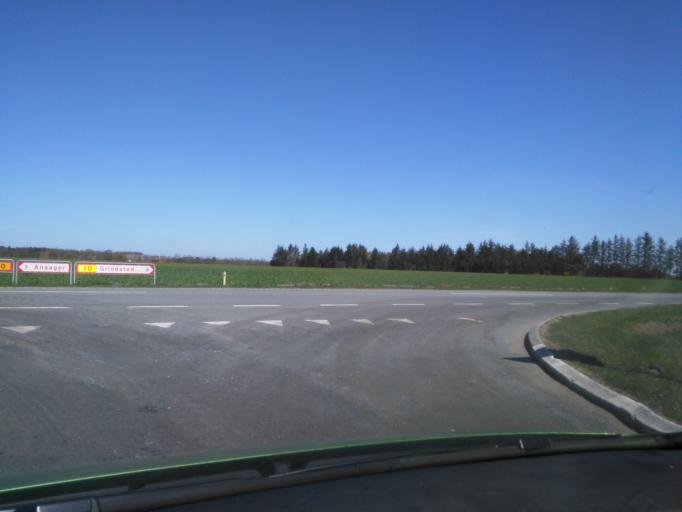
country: DK
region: South Denmark
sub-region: Billund Kommune
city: Grindsted
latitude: 55.7043
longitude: 8.8479
